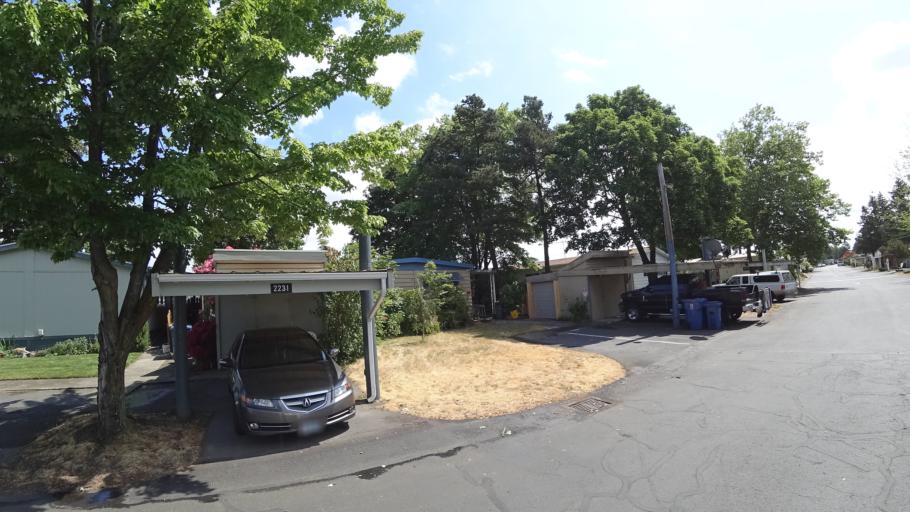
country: US
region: Washington
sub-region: Clark County
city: Vancouver
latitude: 45.6193
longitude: -122.6882
